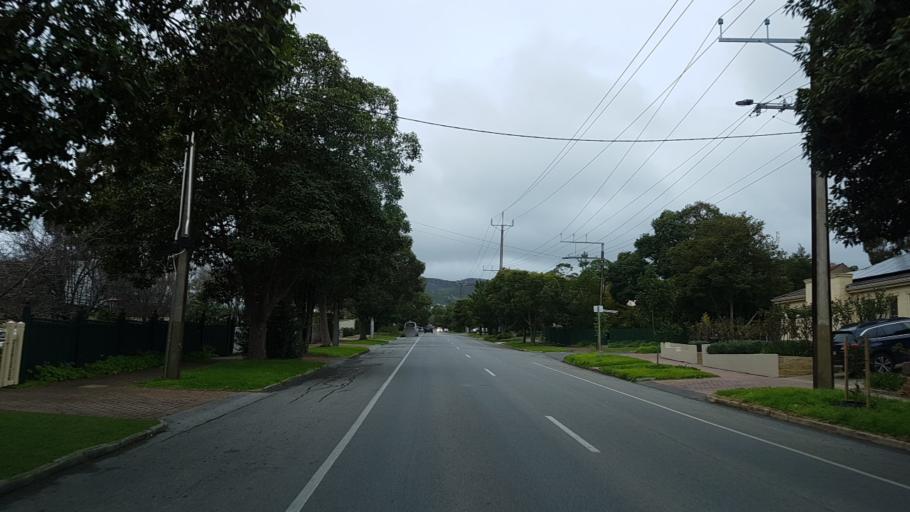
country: AU
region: South Australia
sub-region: Burnside
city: Linden Park
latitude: -34.9451
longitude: 138.6523
